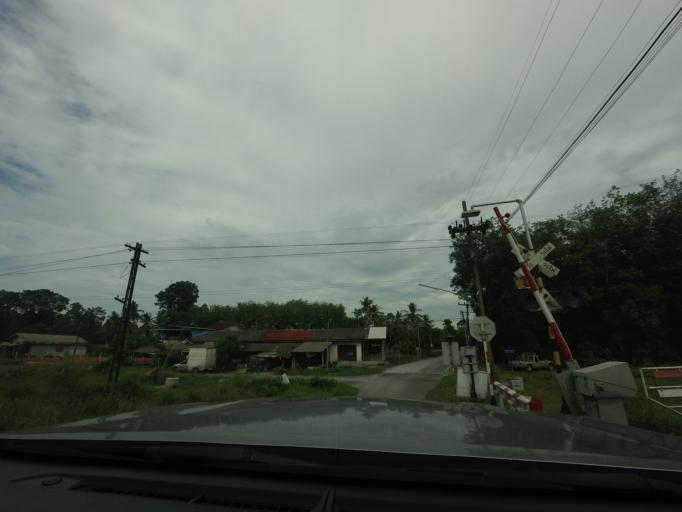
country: TH
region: Nakhon Si Thammarat
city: Phra Phrom
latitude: 8.2792
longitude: 99.9436
